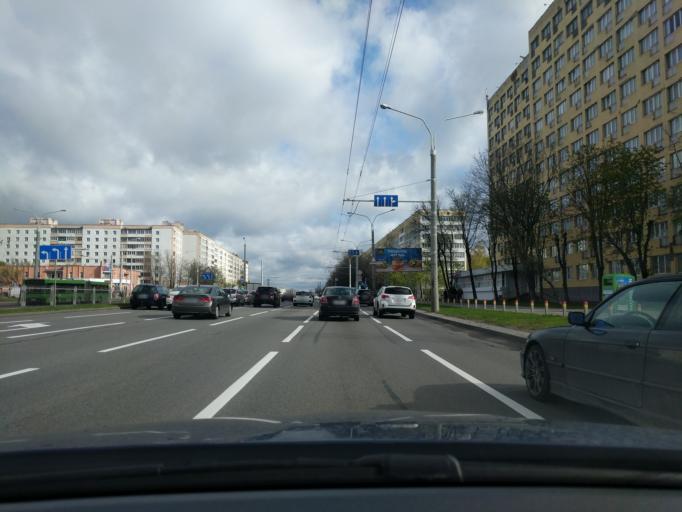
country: BY
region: Minsk
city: Novoye Medvezhino
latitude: 53.9019
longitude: 27.4968
